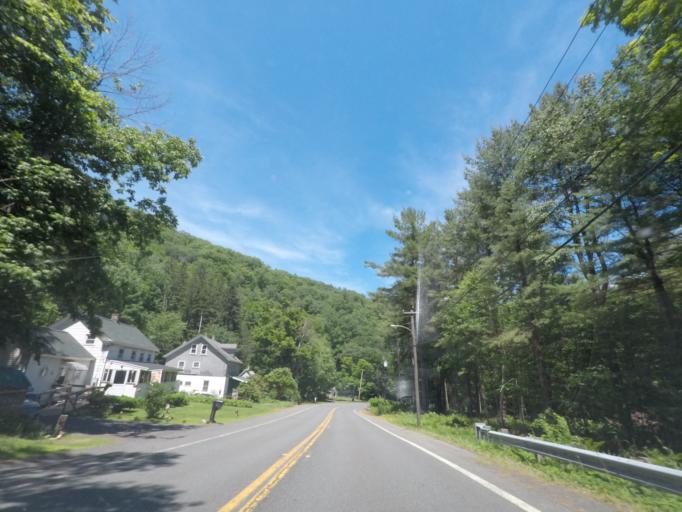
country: US
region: Massachusetts
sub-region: Berkshire County
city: Becket
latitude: 42.2757
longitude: -72.9930
